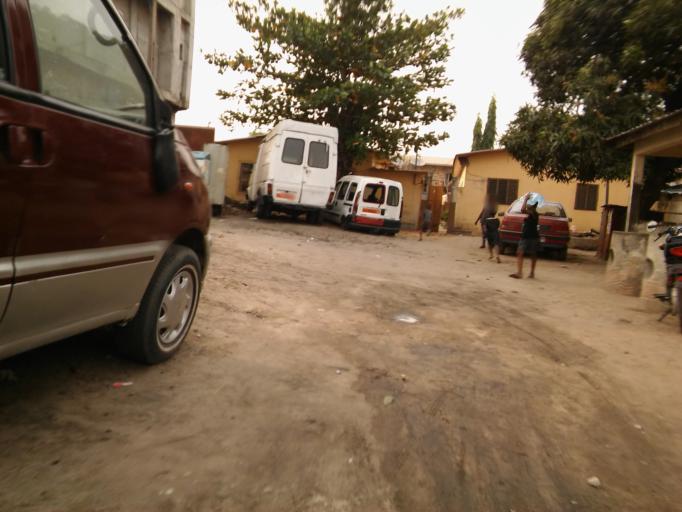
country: BJ
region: Littoral
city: Cotonou
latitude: 6.3589
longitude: 2.4072
